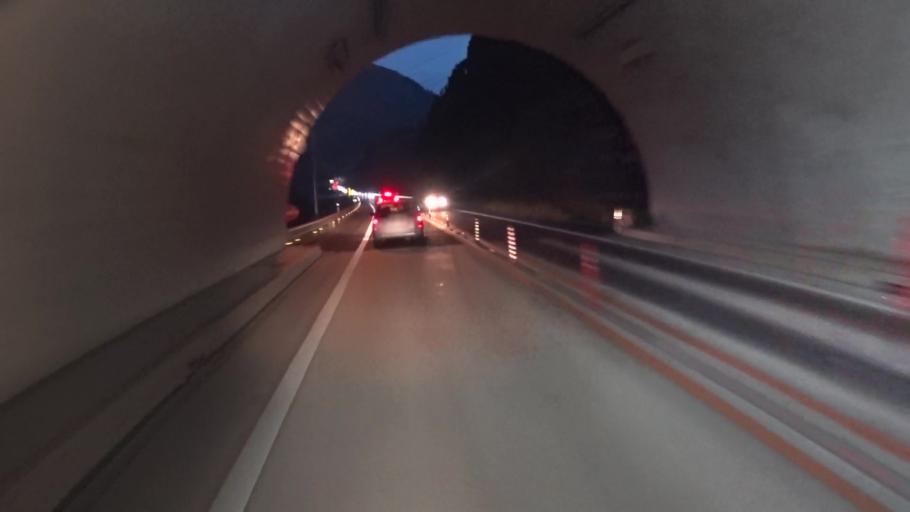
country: JP
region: Kyoto
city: Ayabe
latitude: 35.3159
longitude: 135.3199
